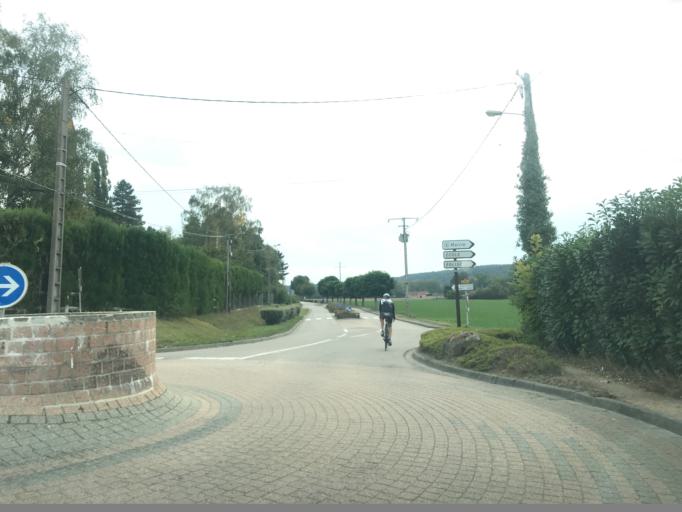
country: FR
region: Haute-Normandie
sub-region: Departement de l'Eure
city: Acquigny
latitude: 49.1927
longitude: 1.1836
